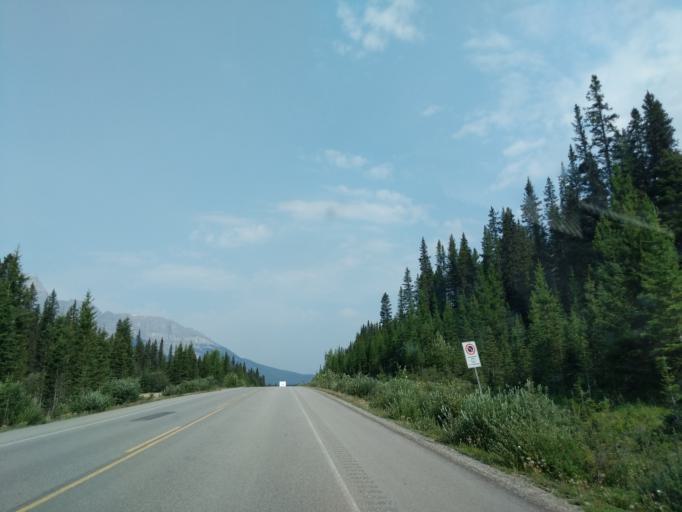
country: CA
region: Alberta
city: Lake Louise
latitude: 51.8699
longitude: -116.6706
